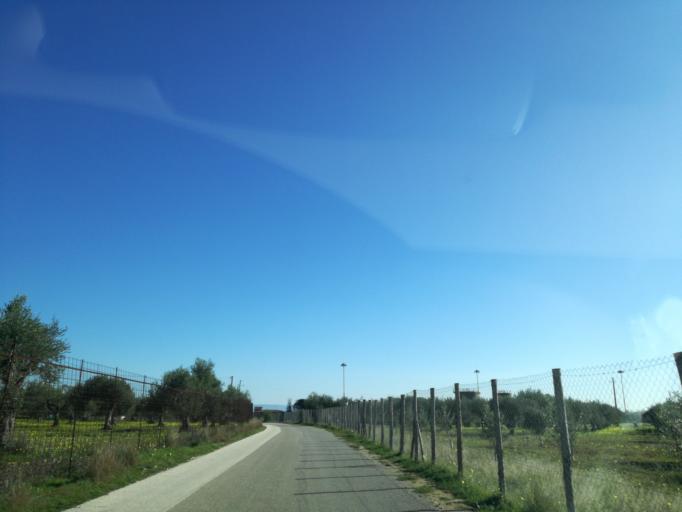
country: IT
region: Sicily
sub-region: Provincia di Caltanissetta
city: Niscemi
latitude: 37.0596
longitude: 14.3553
